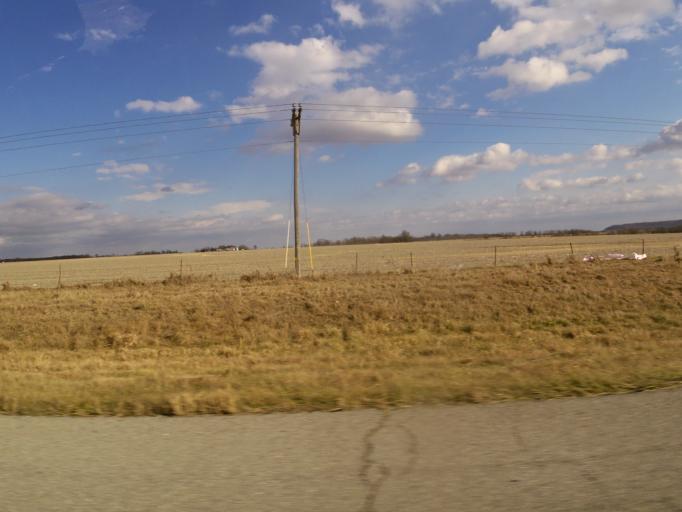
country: US
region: Missouri
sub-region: Pike County
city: Bowling Green
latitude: 39.2951
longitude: -91.1110
